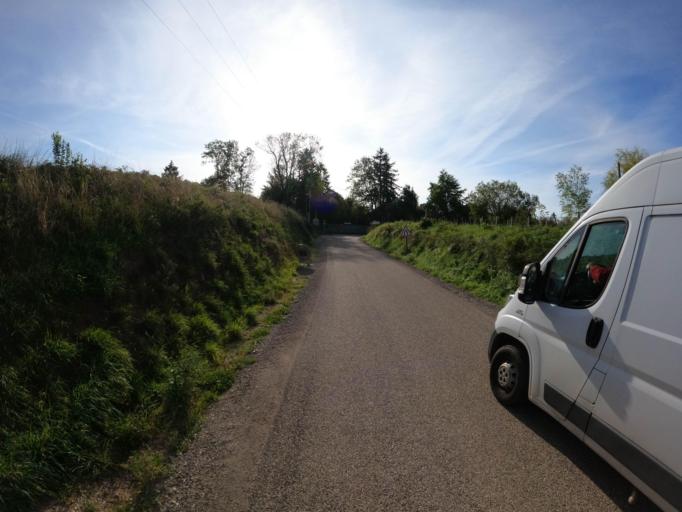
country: FR
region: Franche-Comte
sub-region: Departement du Jura
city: Montmorot
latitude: 46.6880
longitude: 5.5371
